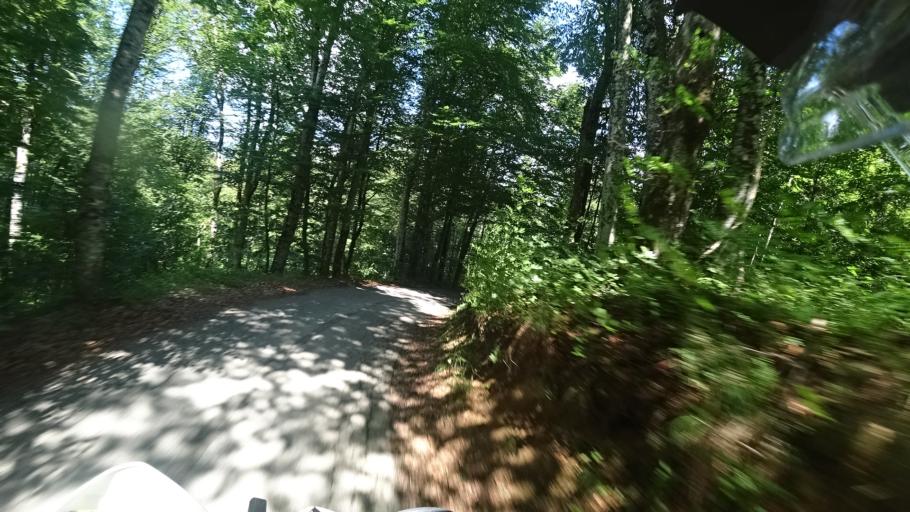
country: SI
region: Osilnica
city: Osilnica
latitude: 45.5142
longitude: 14.6960
